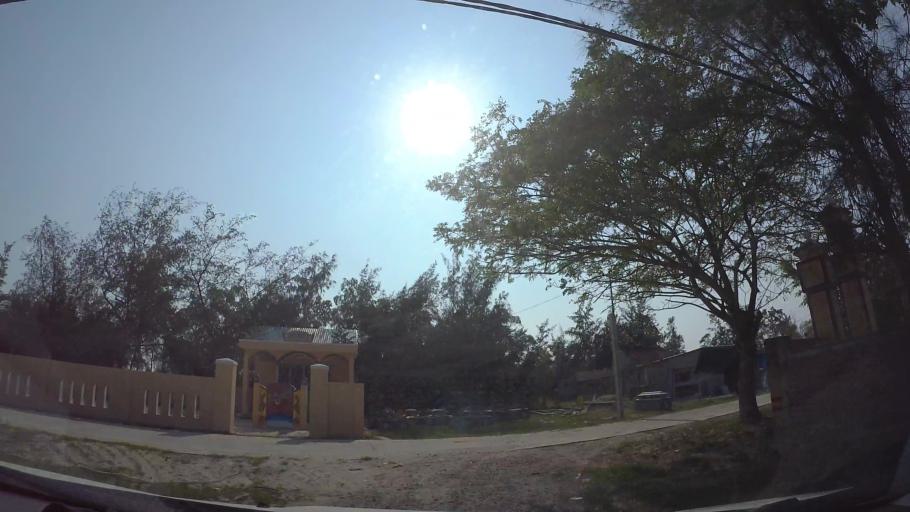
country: VN
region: Quang Nam
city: Quang Nam
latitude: 15.9463
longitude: 108.2714
